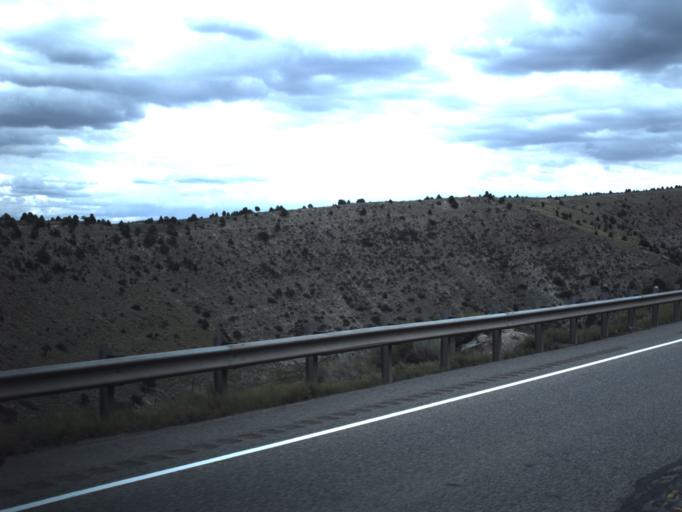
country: US
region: Utah
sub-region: Carbon County
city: Helper
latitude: 39.8194
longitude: -110.9425
